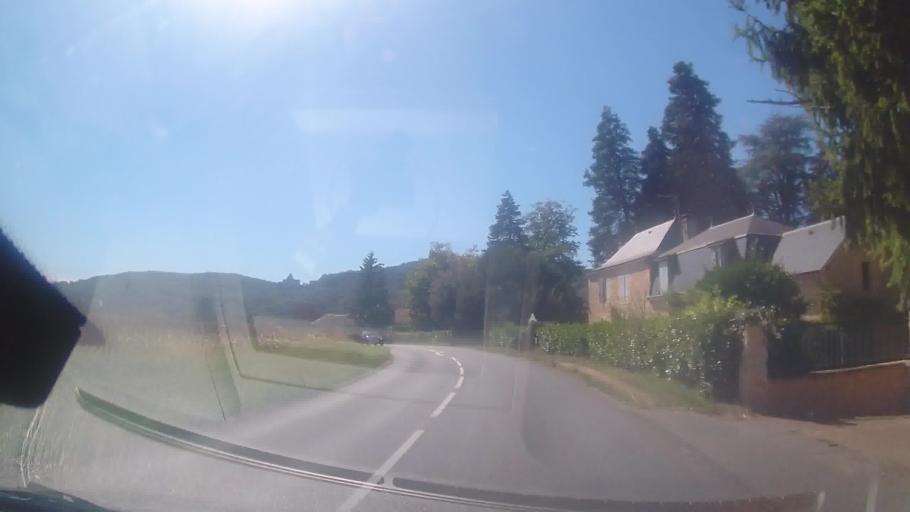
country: FR
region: Aquitaine
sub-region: Departement de la Dordogne
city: Cenac-et-Saint-Julien
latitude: 44.8256
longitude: 1.1582
